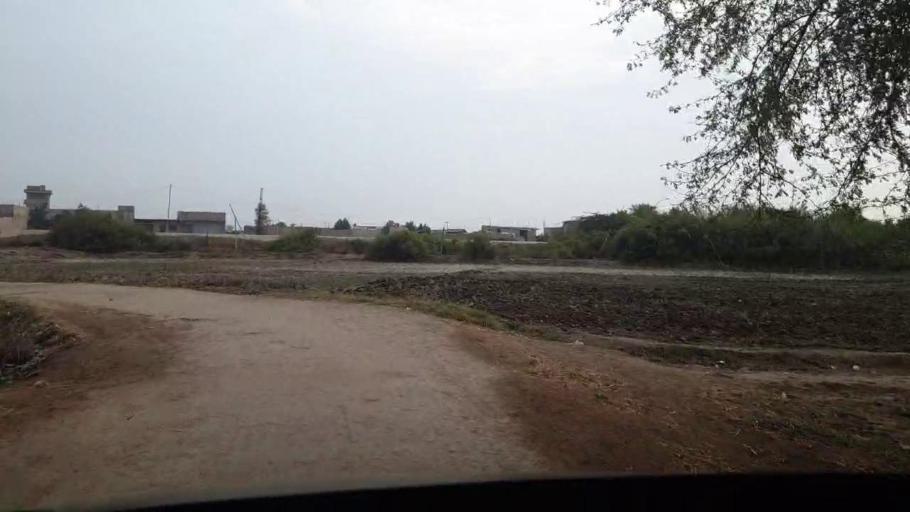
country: PK
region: Sindh
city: Thatta
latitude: 24.5980
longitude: 68.0823
